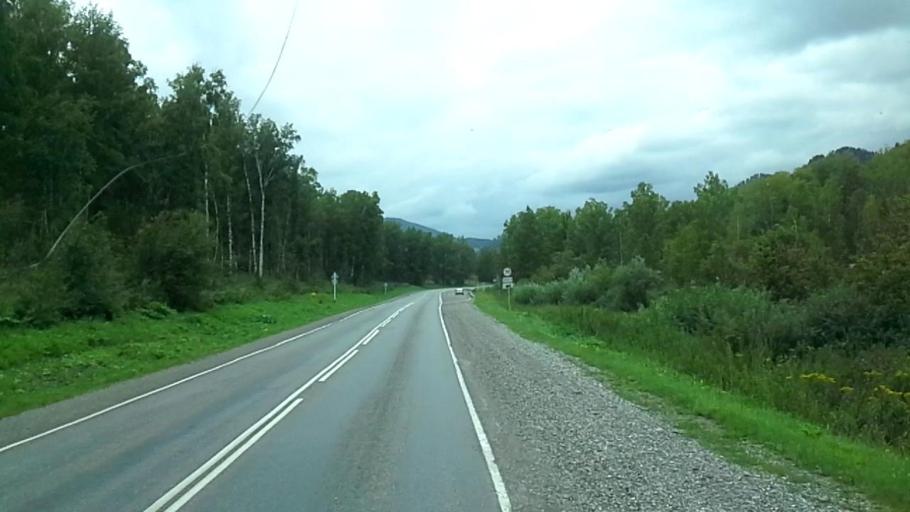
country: RU
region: Altay
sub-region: Mayminskiy Rayon
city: Manzherok
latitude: 51.8580
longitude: 85.7559
